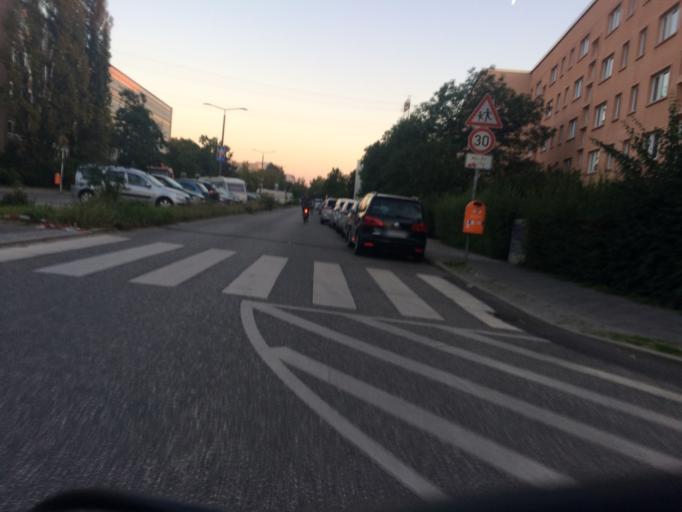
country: DE
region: Berlin
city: Heinersdorf
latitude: 52.5587
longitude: 13.4226
